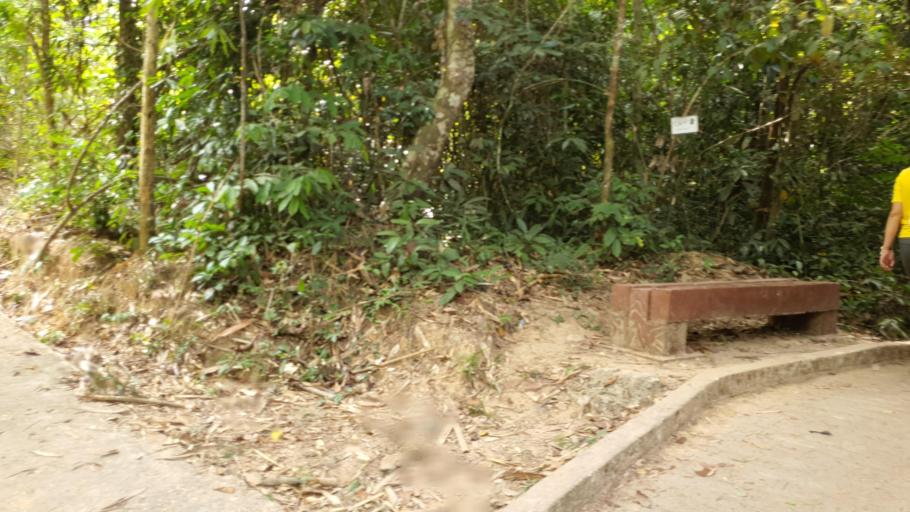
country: TH
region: Nakhon Phanom
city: Ban Phaeng
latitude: 17.9843
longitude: 104.1311
